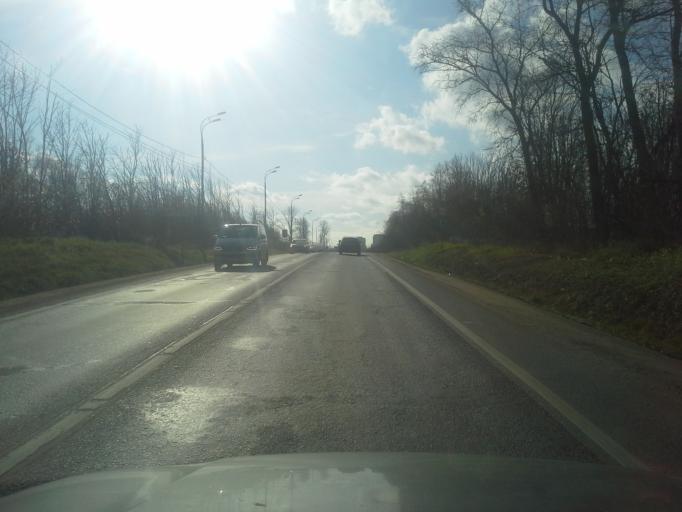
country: RU
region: Moskovskaya
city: Bol'shiye Vyazemy
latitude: 55.6364
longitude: 36.9838
